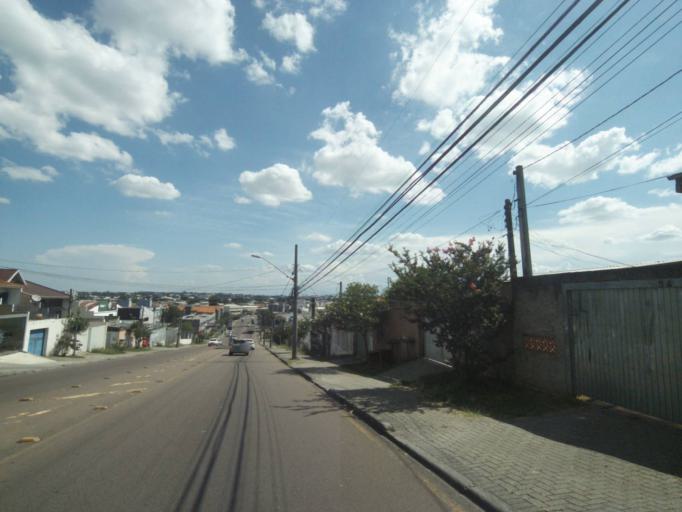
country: BR
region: Parana
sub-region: Pinhais
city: Pinhais
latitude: -25.4740
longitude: -49.2389
